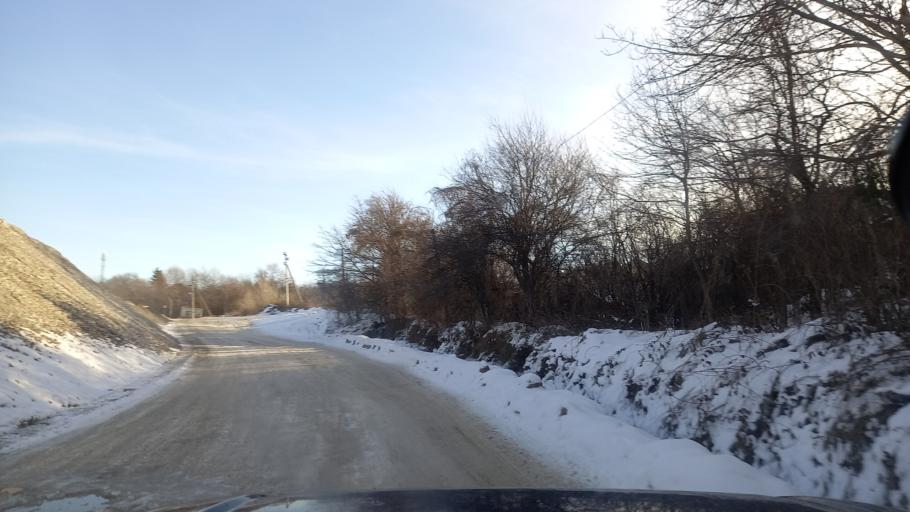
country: RU
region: Adygeya
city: Kamennomostskiy
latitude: 44.2900
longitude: 40.1814
